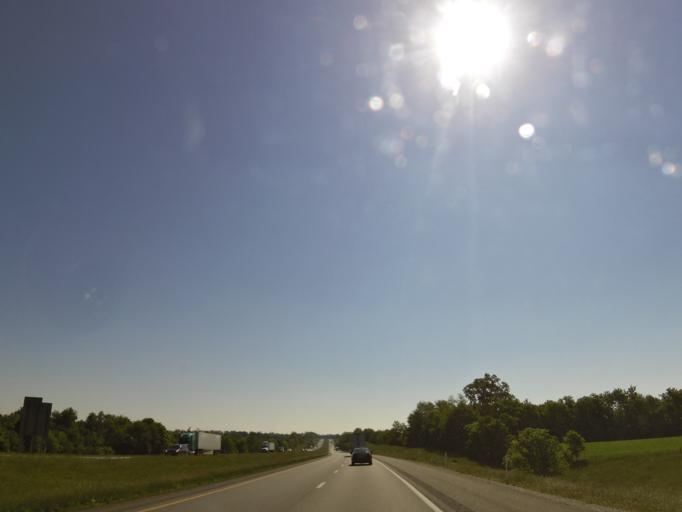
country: US
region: Kentucky
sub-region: Woodford County
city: Midway
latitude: 38.1589
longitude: -84.6554
